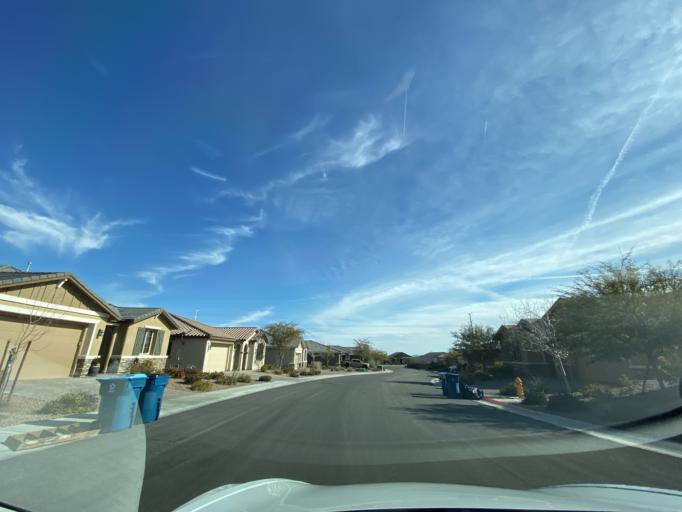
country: US
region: Nevada
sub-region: Clark County
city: Summerlin South
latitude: 36.2905
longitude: -115.3310
